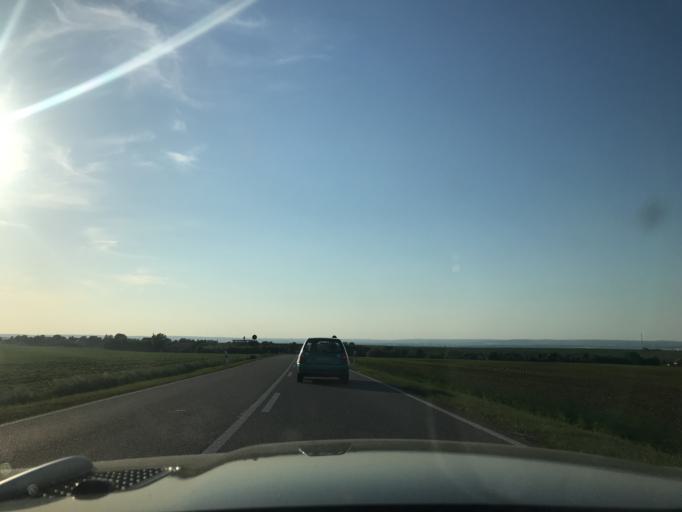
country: DE
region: Thuringia
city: Bad Langensalza
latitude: 51.0637
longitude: 10.6455
